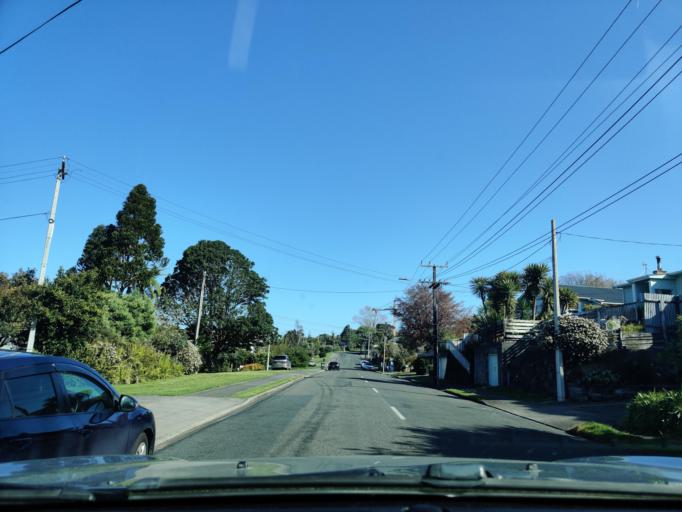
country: NZ
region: Taranaki
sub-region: New Plymouth District
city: New Plymouth
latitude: -39.0656
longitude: 174.0543
